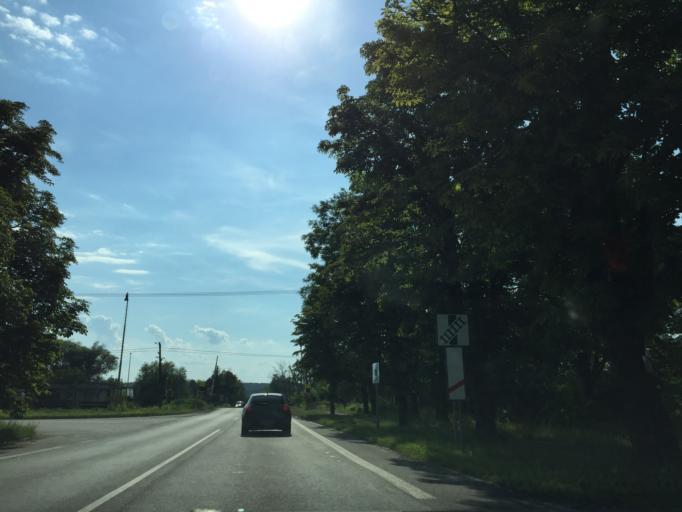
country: SK
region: Kosicky
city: Strazske
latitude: 48.8715
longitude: 21.8260
